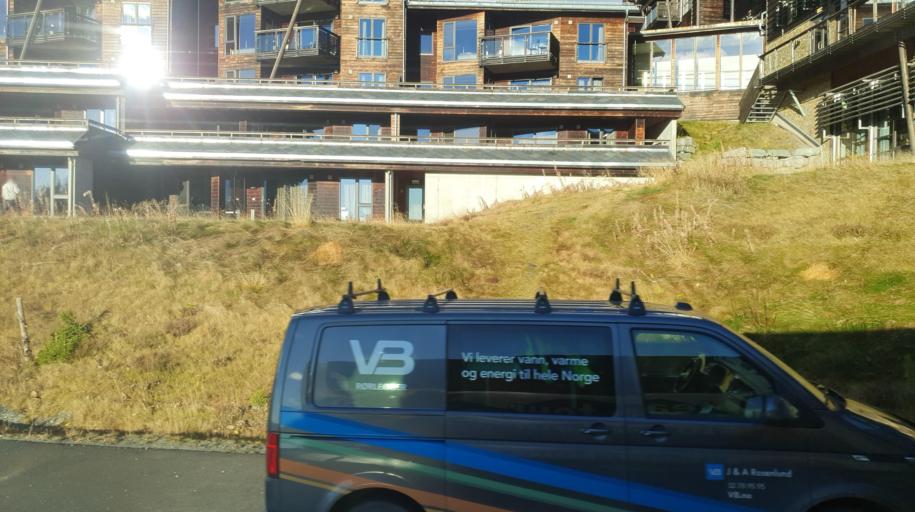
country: NO
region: Buskerud
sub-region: Krodsherad
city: Noresund
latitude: 60.2266
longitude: 9.5198
